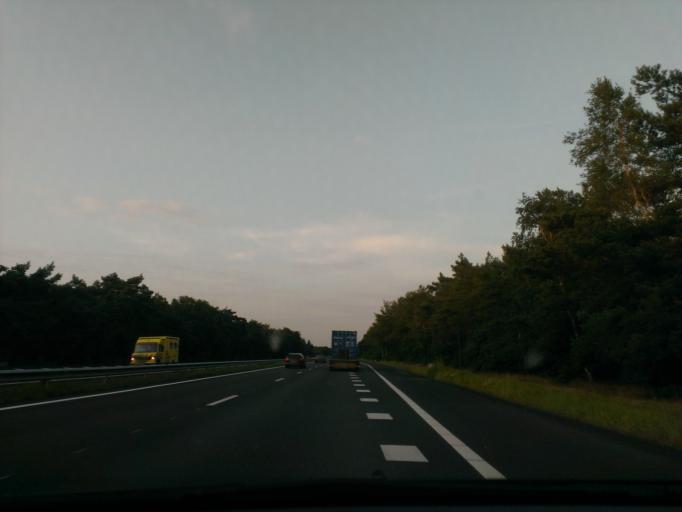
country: NL
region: Gelderland
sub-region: Gemeente Oldebroek
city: Oldebroek
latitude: 52.4053
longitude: 5.8816
